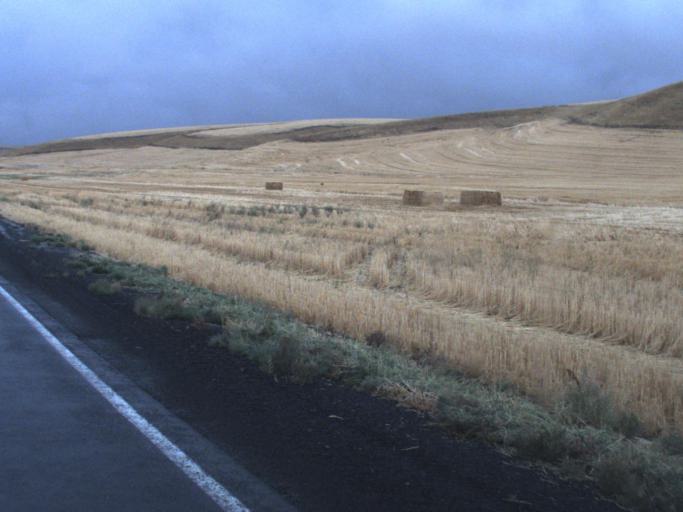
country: US
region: Washington
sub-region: Spokane County
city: Cheney
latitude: 47.1444
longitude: -117.8347
